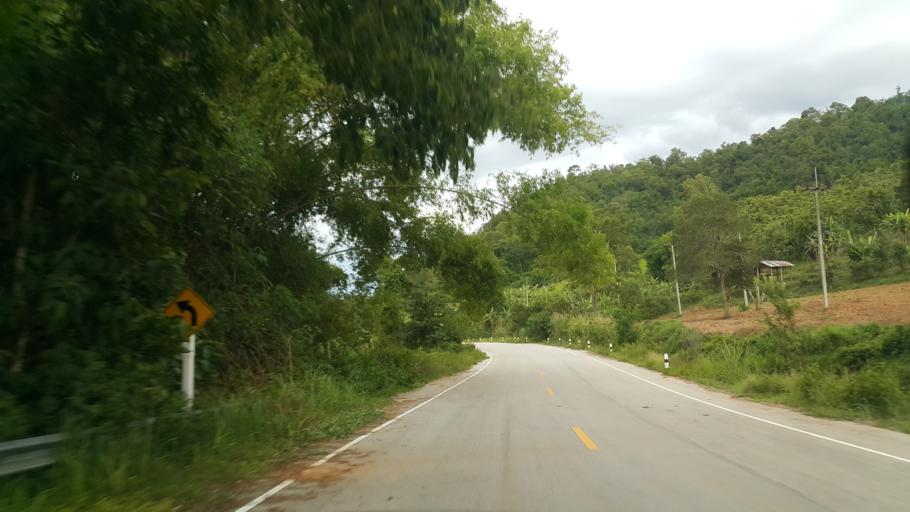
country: TH
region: Loei
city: Na Haeo
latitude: 17.4938
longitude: 101.0965
